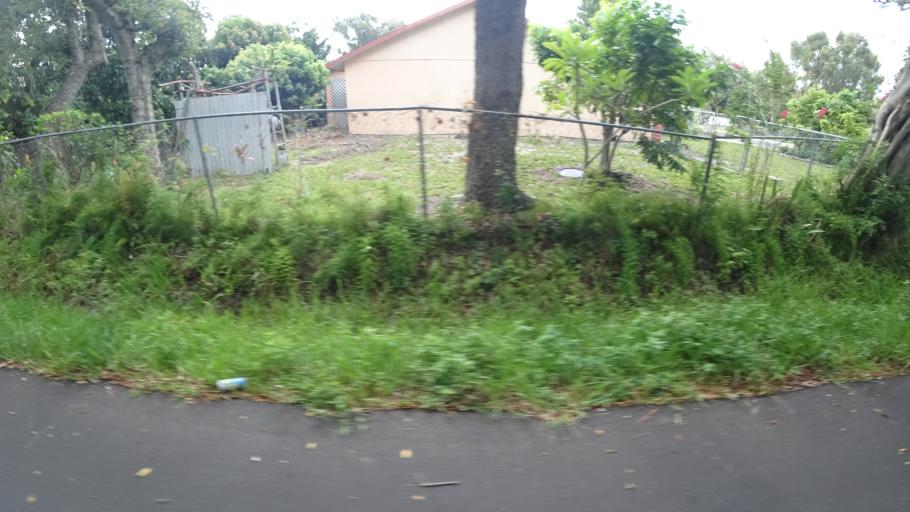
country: US
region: Florida
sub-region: Manatee County
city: Whitfield
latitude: 27.4163
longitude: -82.5509
